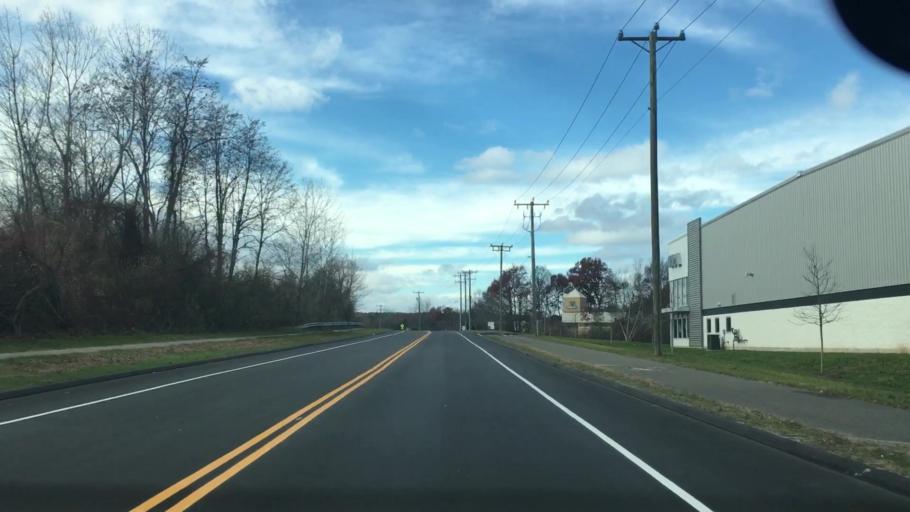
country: US
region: Connecticut
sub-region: Hartford County
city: Plainville
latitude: 41.6937
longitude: -72.8576
